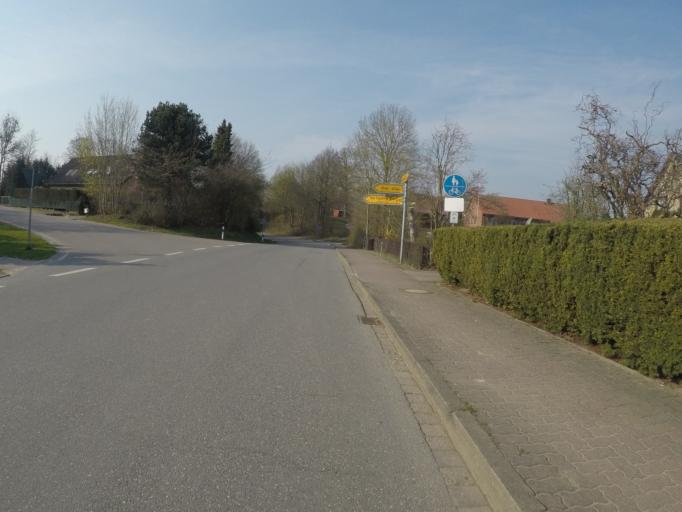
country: DE
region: Schleswig-Holstein
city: Gross Niendorf
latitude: 53.8501
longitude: 10.2433
